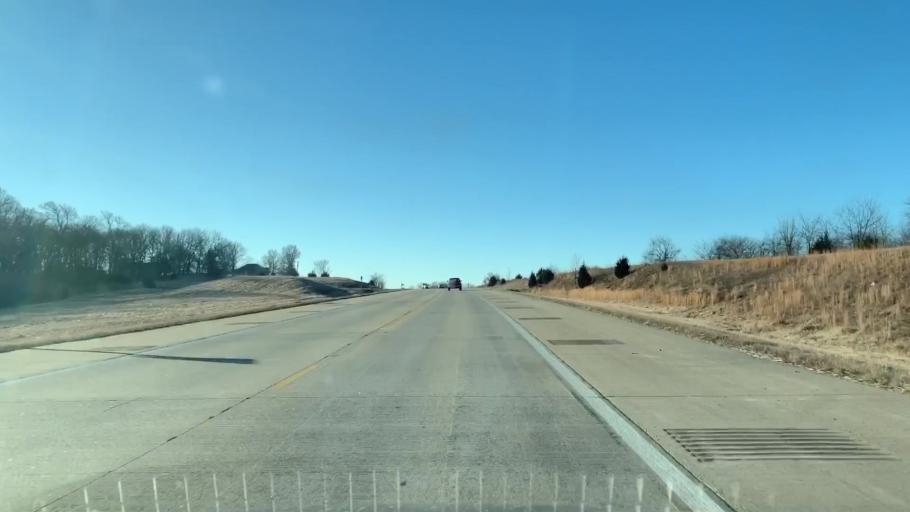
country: US
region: Kansas
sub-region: Crawford County
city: Arma
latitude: 37.5815
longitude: -94.7057
